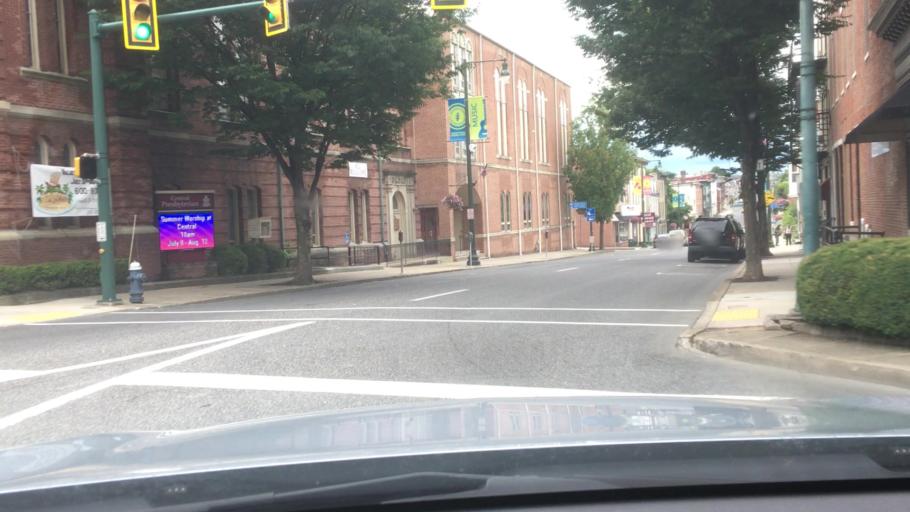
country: US
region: Pennsylvania
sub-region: Franklin County
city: Chambersburg
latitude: 39.9376
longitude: -77.6615
